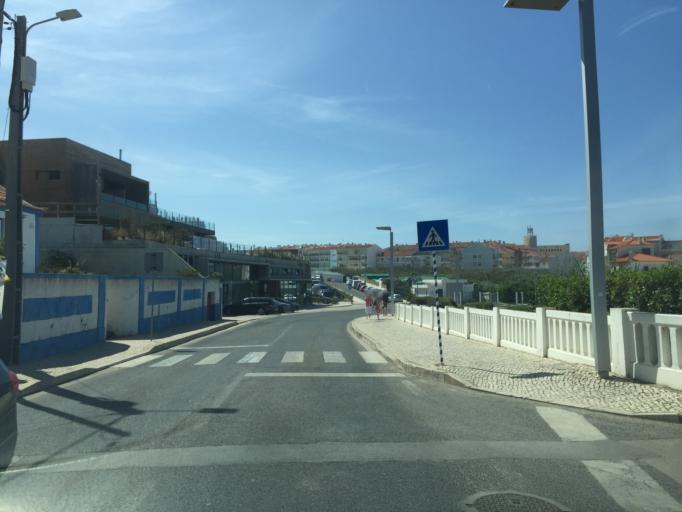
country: PT
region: Lisbon
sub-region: Torres Vedras
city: Silveira
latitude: 39.1373
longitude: -9.3791
